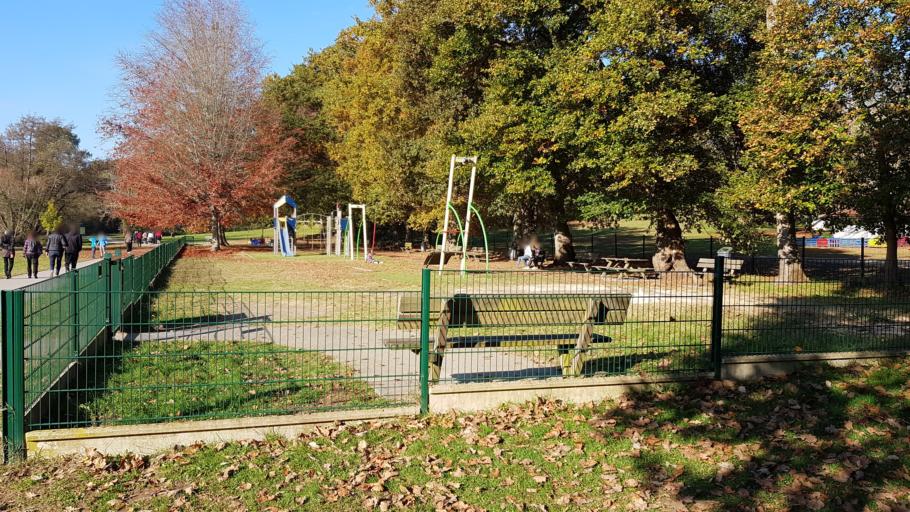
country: FR
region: Aquitaine
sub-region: Departement des Landes
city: Saint-Paul-les-Dax
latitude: 43.7315
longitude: -1.0698
